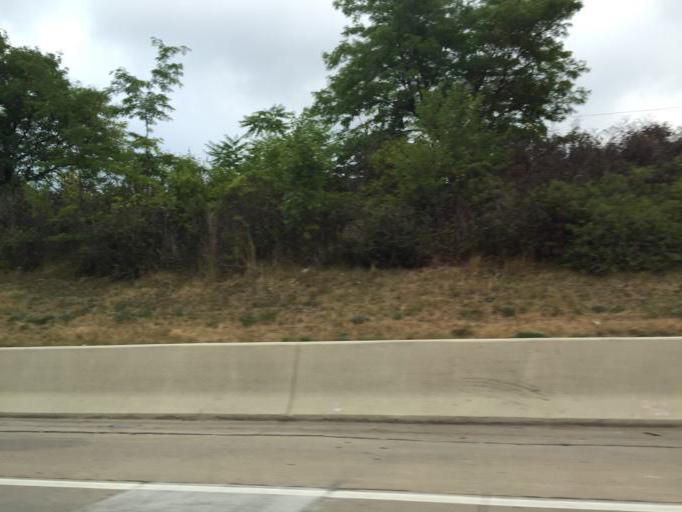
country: US
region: Michigan
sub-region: Wayne County
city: Highland Park
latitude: 42.3711
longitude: -83.0843
